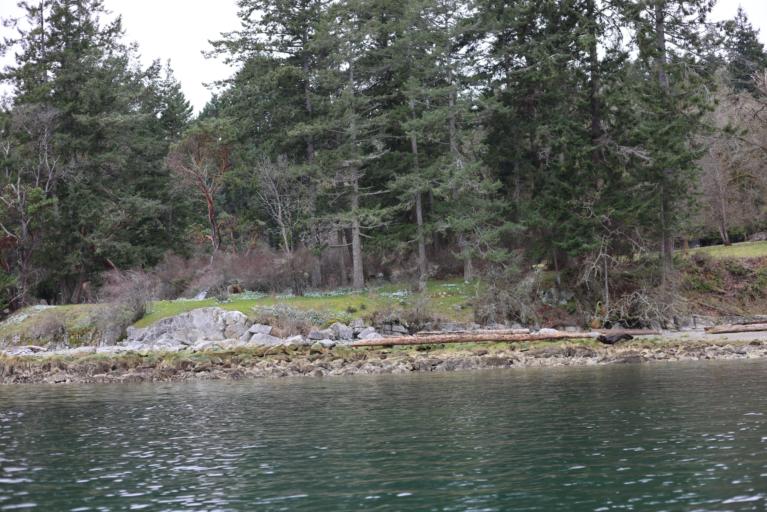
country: CA
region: British Columbia
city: North Saanich
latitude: 48.6564
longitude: -123.5373
